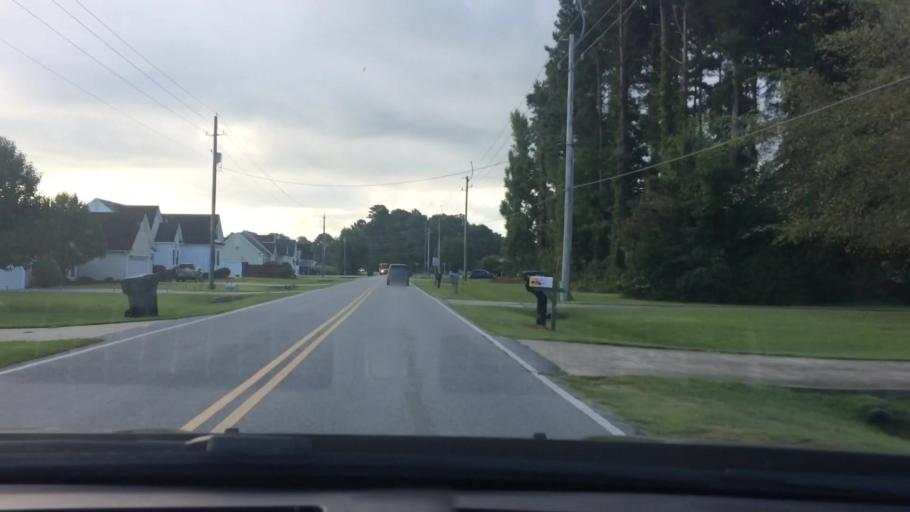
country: US
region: North Carolina
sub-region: Pitt County
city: Winterville
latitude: 35.5386
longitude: -77.3898
